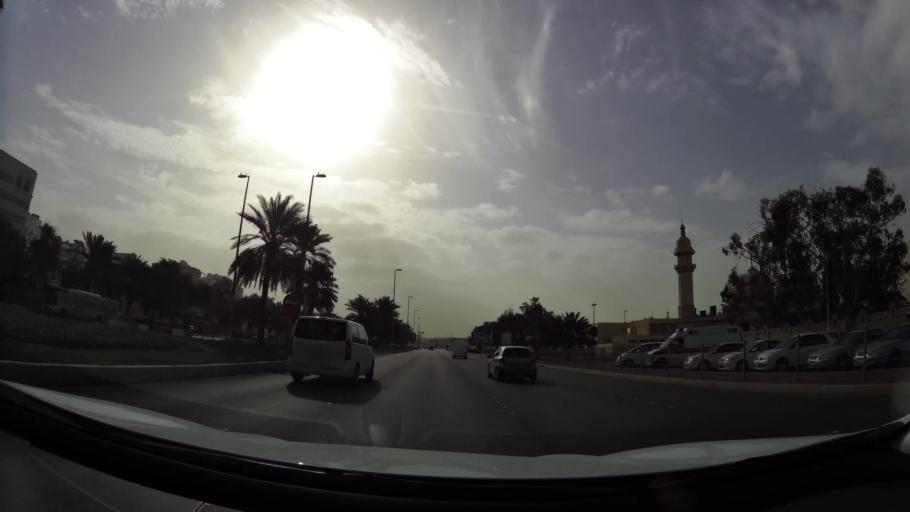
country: AE
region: Abu Dhabi
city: Abu Dhabi
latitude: 24.4449
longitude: 54.4025
